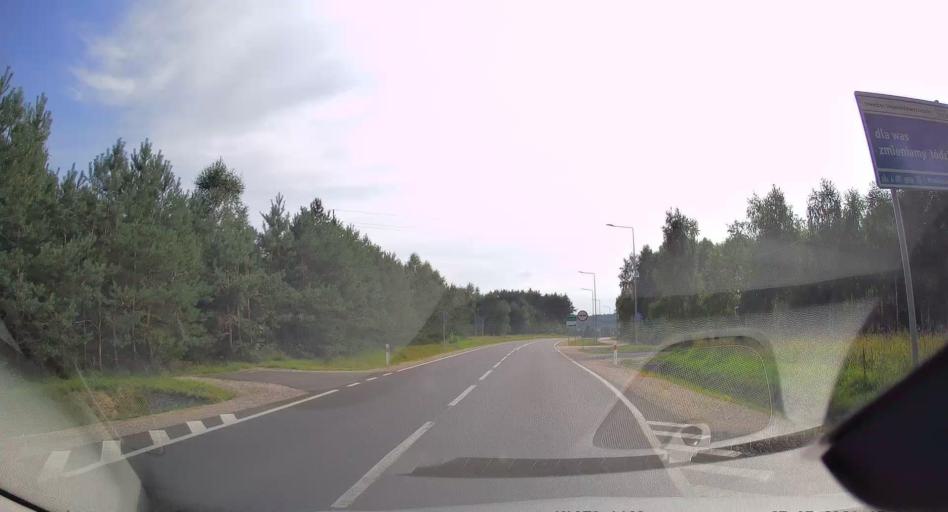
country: PL
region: Lodz Voivodeship
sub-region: Powiat tomaszowski
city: Inowlodz
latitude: 51.5583
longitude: 20.2602
